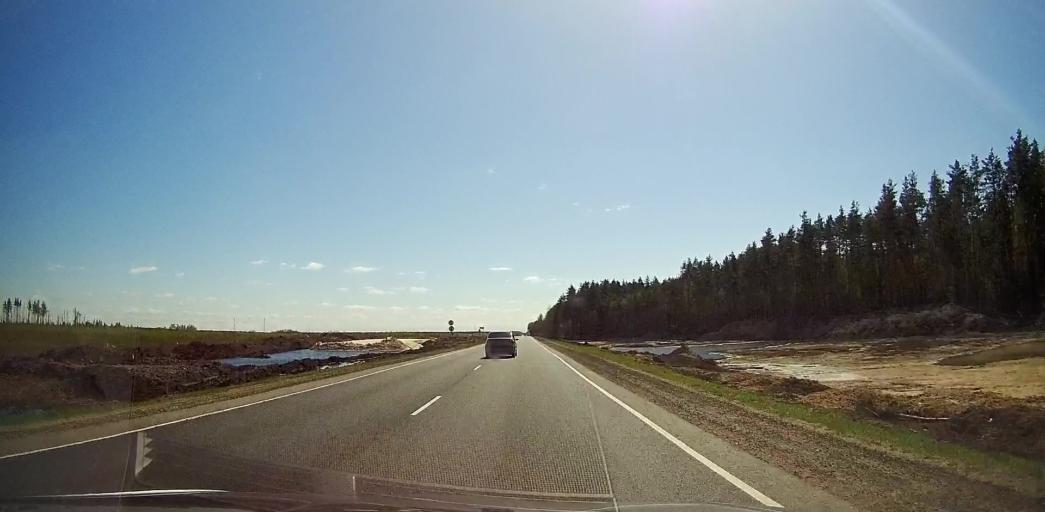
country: RU
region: Moskovskaya
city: Gzhel'
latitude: 55.5945
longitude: 38.3805
